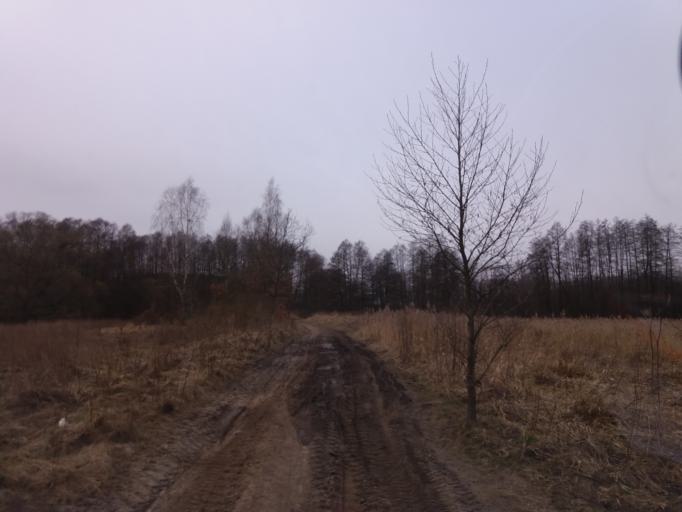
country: PL
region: West Pomeranian Voivodeship
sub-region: Powiat choszczenski
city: Bierzwnik
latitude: 53.1556
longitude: 15.6220
